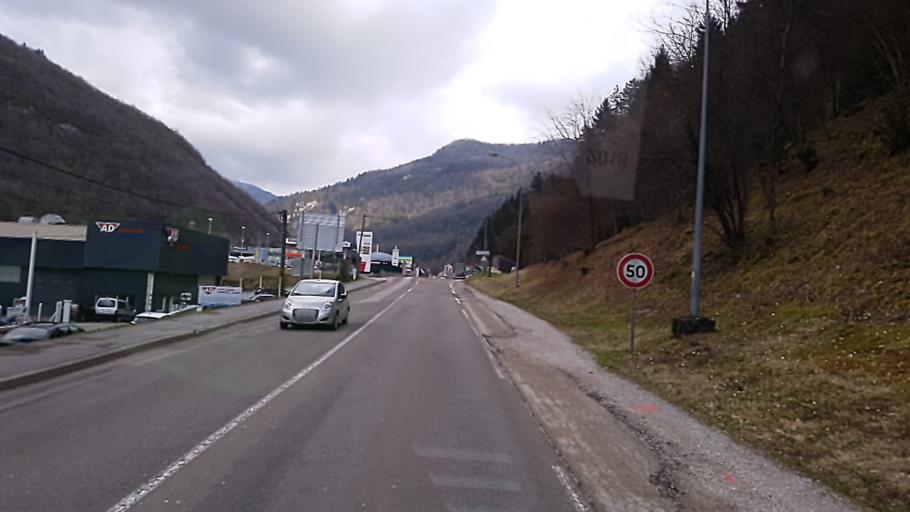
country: FR
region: Franche-Comte
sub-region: Departement du Jura
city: Saint-Claude
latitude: 46.3808
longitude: 5.8320
